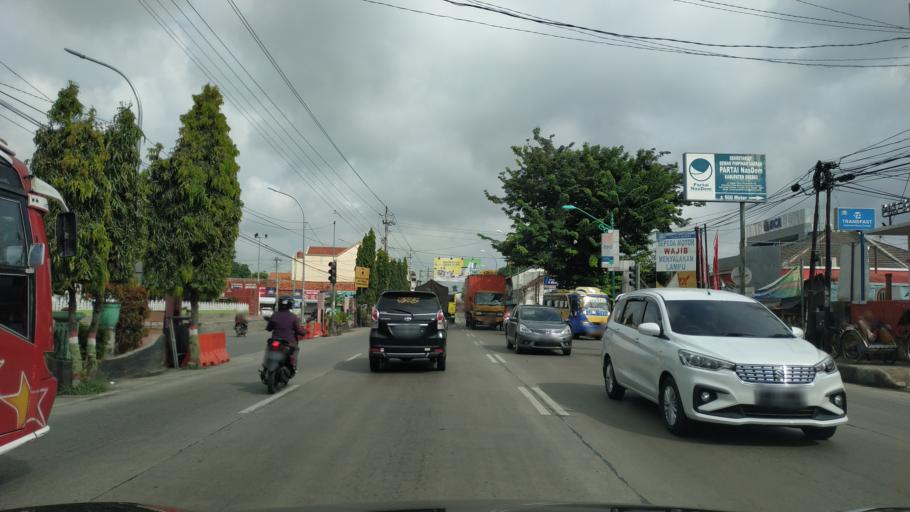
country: ID
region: Central Java
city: Dukuhturi
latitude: -6.8702
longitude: 109.0372
